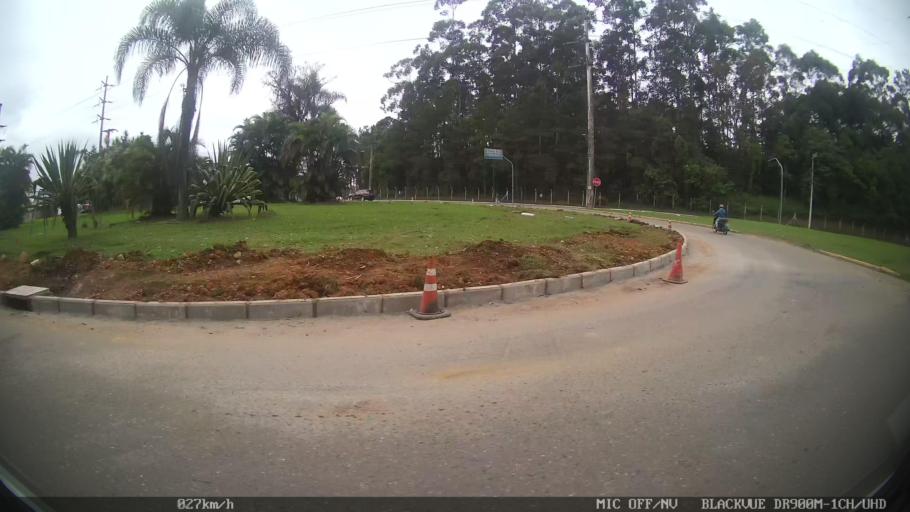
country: BR
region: Santa Catarina
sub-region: Joinville
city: Joinville
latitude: -26.2853
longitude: -48.8106
